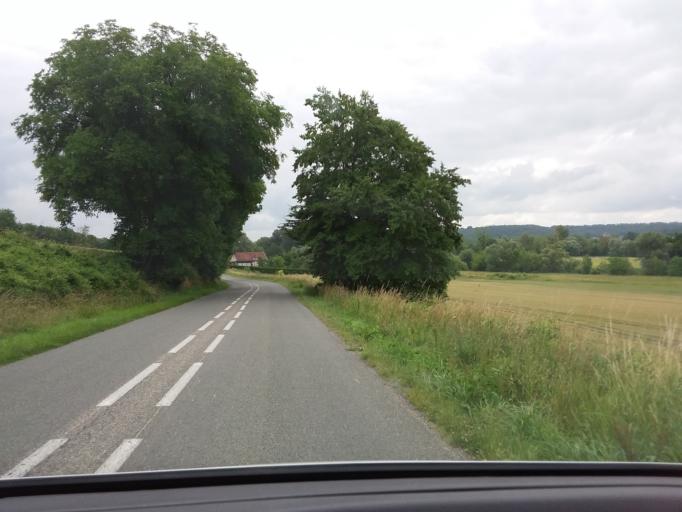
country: FR
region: Picardie
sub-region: Departement de l'Aisne
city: Vailly-sur-Aisne
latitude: 49.4028
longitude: 3.5630
